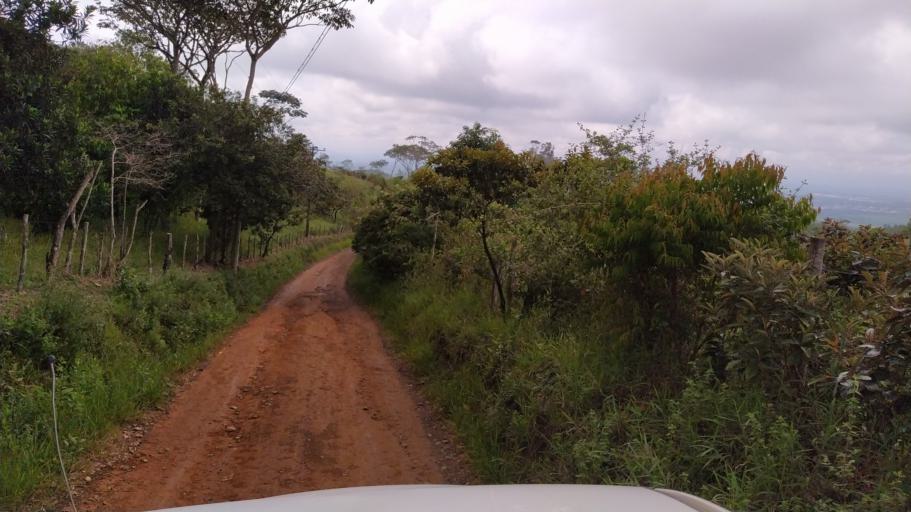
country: CO
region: Valle del Cauca
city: Jamundi
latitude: 3.3231
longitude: -76.5838
